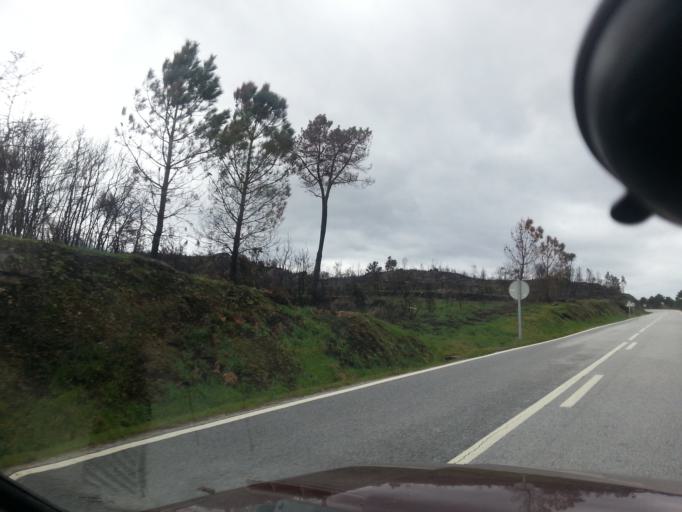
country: PT
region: Guarda
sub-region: Fornos de Algodres
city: Fornos de Algodres
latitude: 40.5786
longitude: -7.5441
